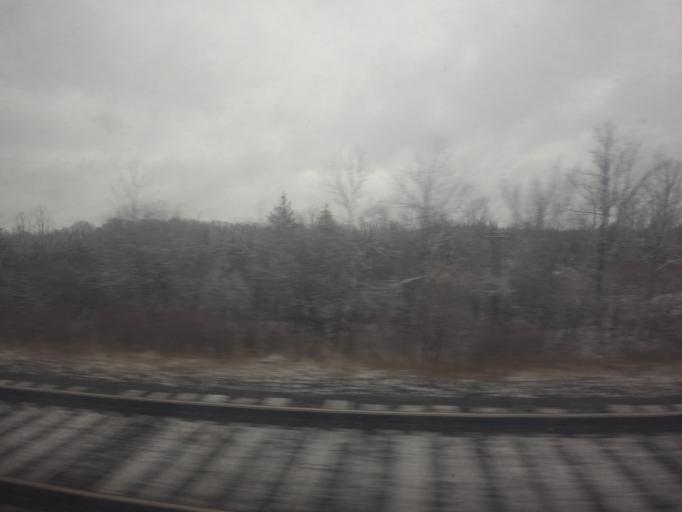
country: US
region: New York
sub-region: Jefferson County
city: Alexandria Bay
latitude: 44.4175
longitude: -75.9937
